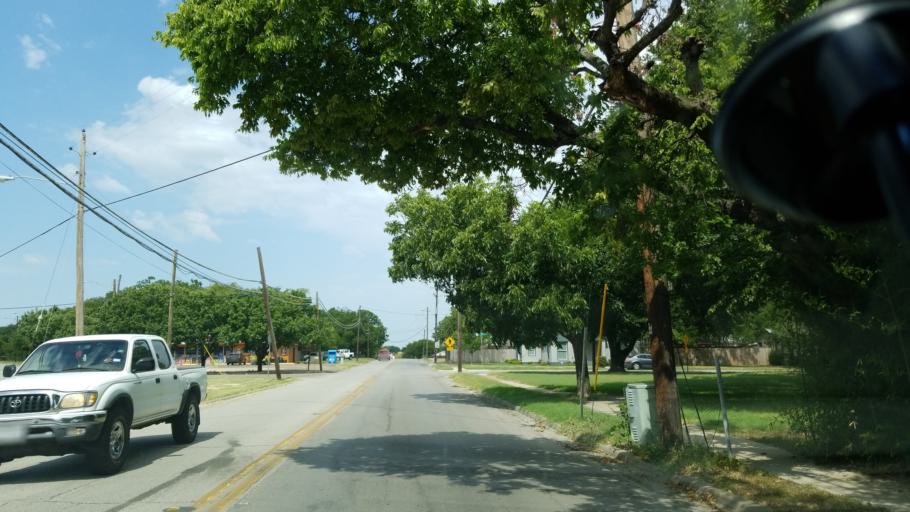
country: US
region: Texas
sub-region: Dallas County
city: Grand Prairie
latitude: 32.7488
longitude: -96.9917
